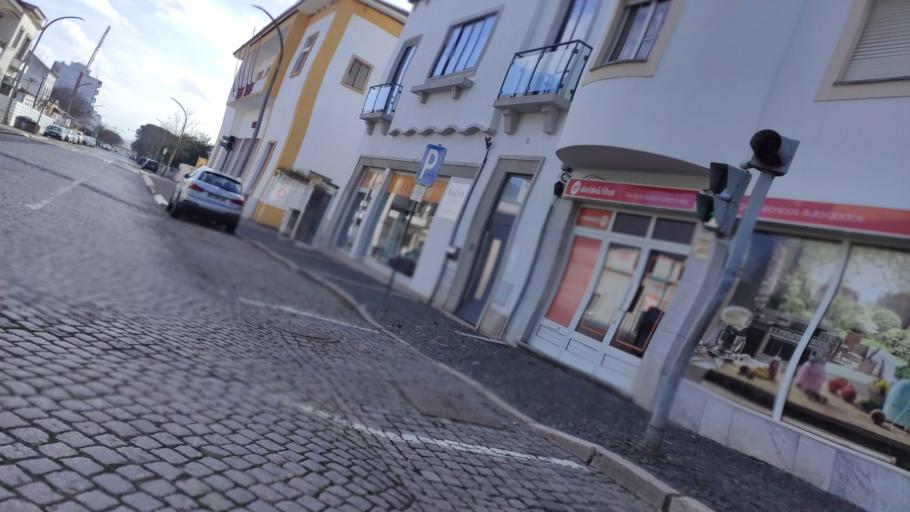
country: PT
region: Beja
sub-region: Beja
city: Beja
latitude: 38.0102
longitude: -7.8645
